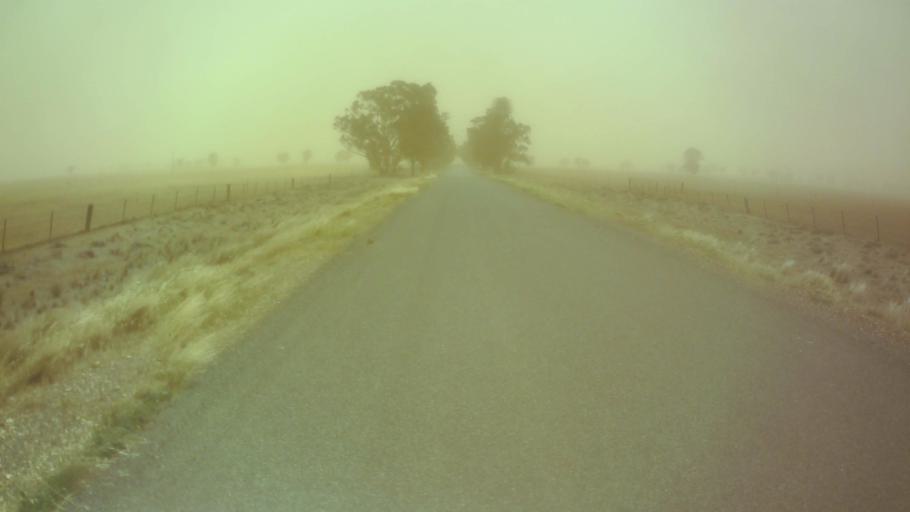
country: AU
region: New South Wales
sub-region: Weddin
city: Grenfell
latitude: -33.7104
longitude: 147.9120
